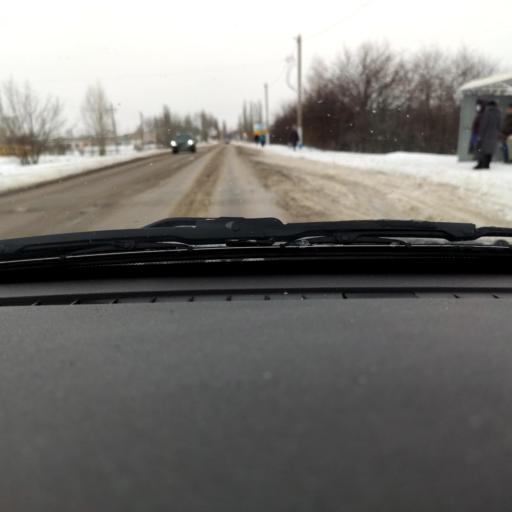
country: RU
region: Voronezj
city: Novaya Usman'
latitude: 51.6088
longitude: 39.3742
